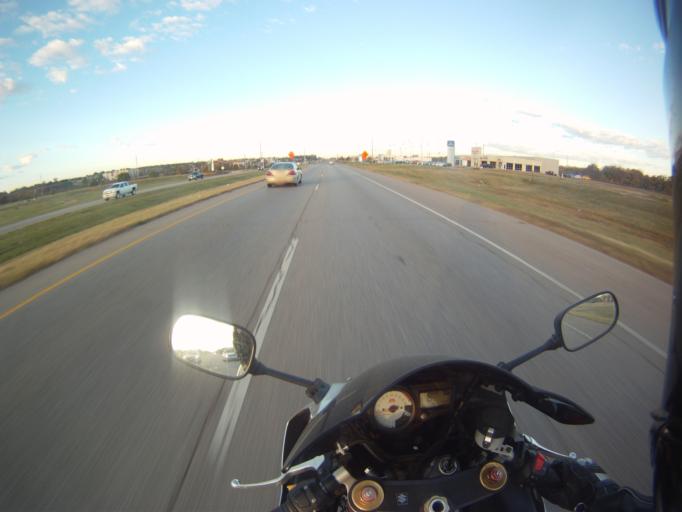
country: US
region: Oklahoma
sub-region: Payne County
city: Stillwater
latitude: 36.1159
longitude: -97.1111
